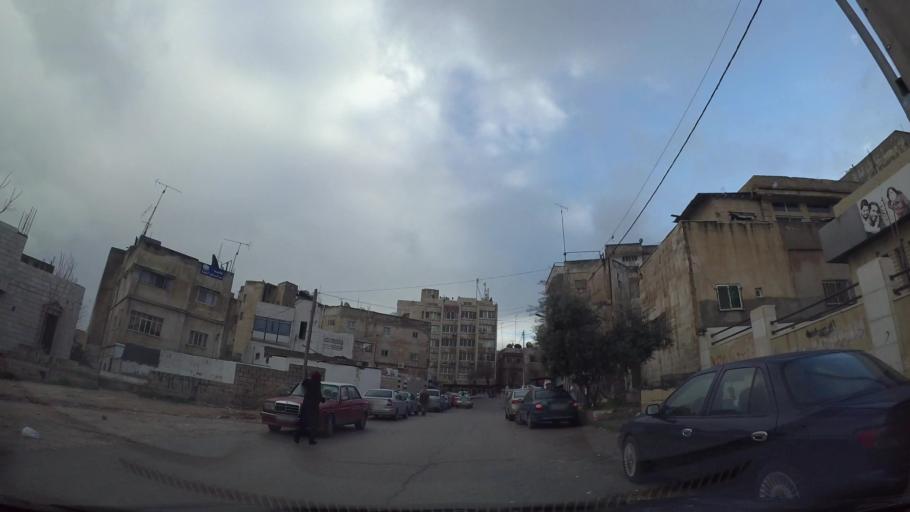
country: JO
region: Amman
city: Amman
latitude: 31.9629
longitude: 35.9253
